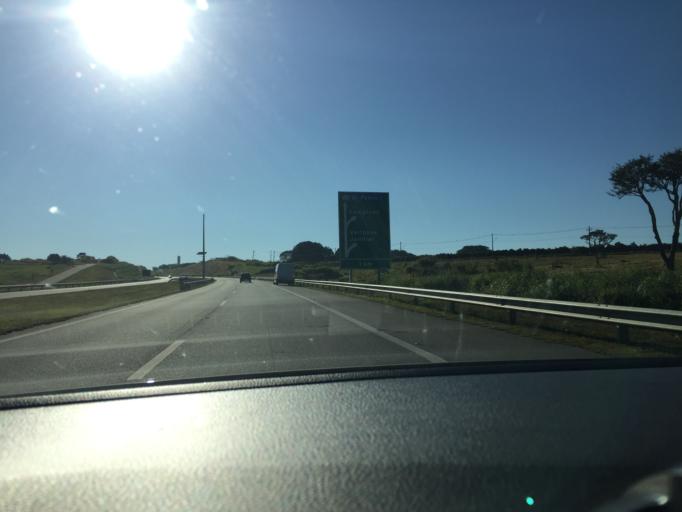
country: BR
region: Sao Paulo
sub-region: Valinhos
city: Valinhos
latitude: -22.9888
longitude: -47.0588
